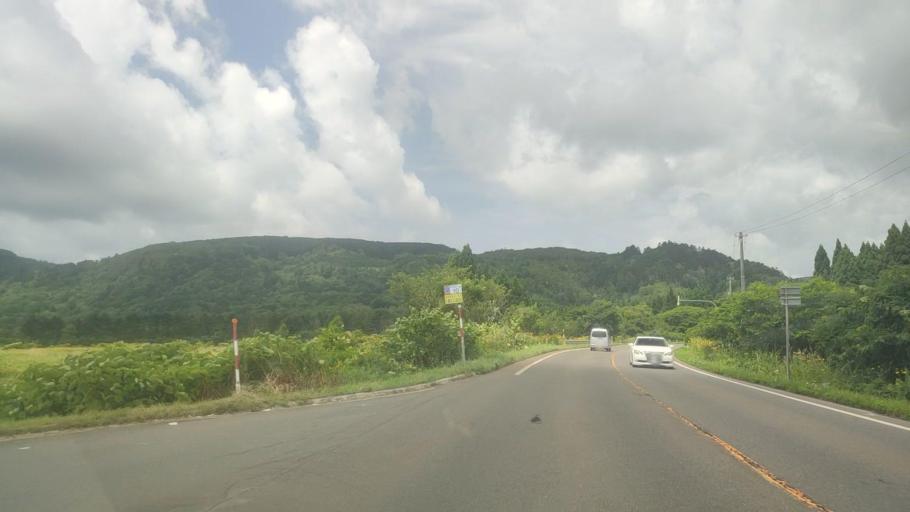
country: JP
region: Hokkaido
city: Niseko Town
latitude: 42.5862
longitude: 140.4499
